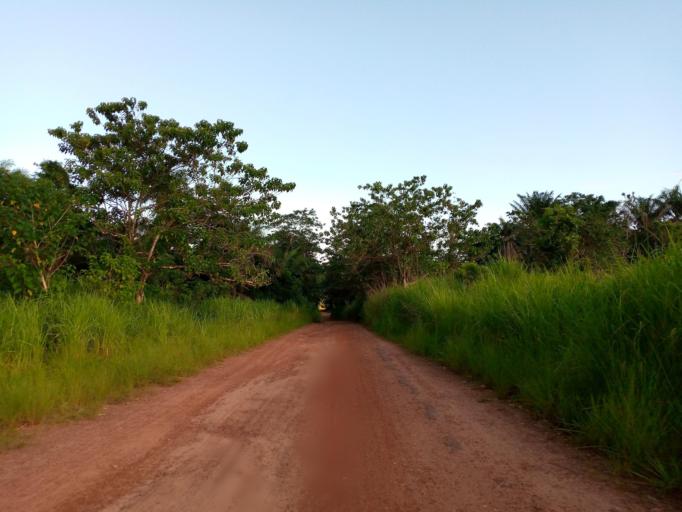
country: SL
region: Northern Province
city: Yonibana
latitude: 8.4560
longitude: -12.2467
